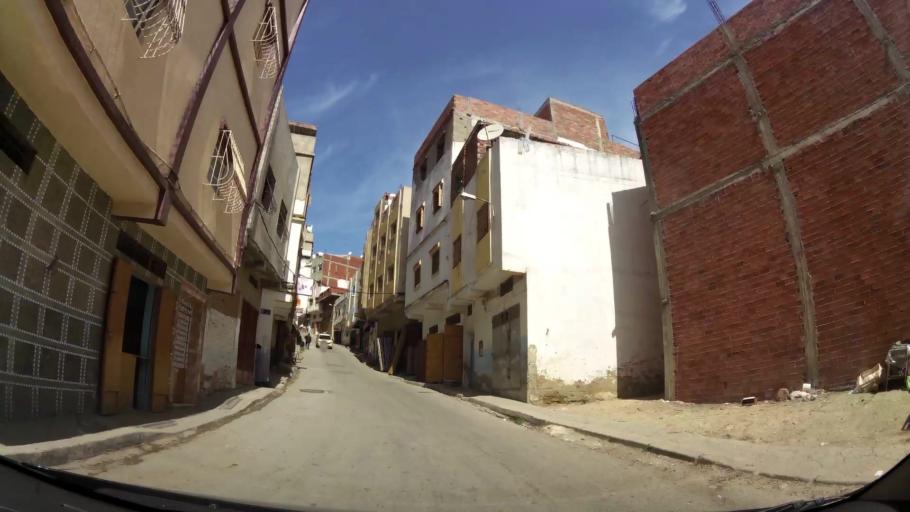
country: MA
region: Tanger-Tetouan
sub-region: Tanger-Assilah
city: Tangier
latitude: 35.7388
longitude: -5.8093
